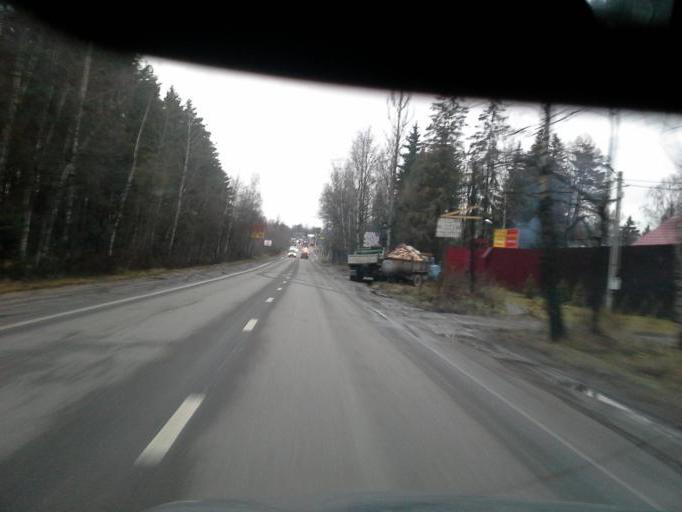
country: RU
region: Moskovskaya
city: Zhavoronki
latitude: 55.6357
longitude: 37.0985
